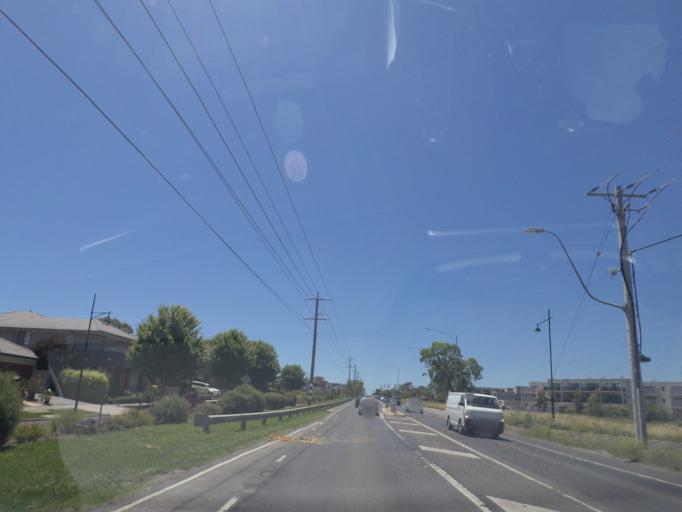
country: AU
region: Victoria
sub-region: Whittlesea
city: Epping
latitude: -37.6318
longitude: 145.0273
